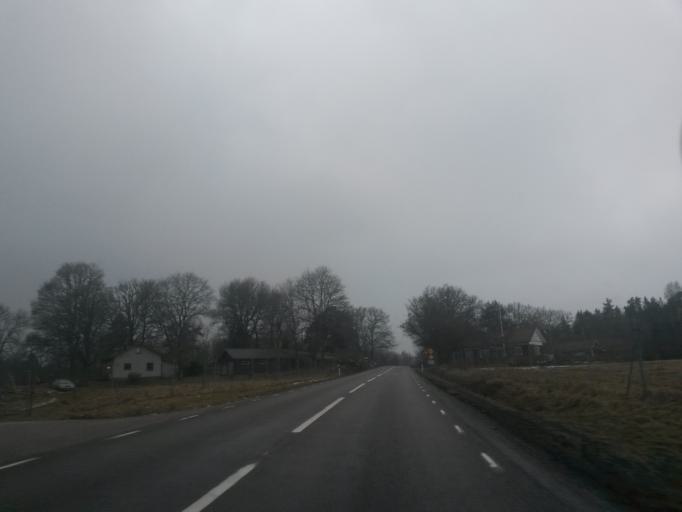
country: SE
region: Vaestra Goetaland
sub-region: Alingsas Kommun
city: Sollebrunn
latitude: 58.1382
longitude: 12.4264
